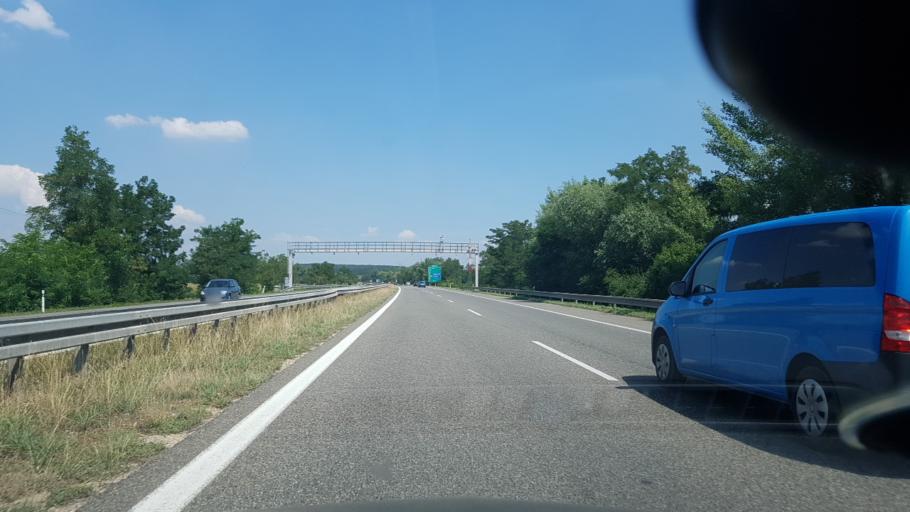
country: CZ
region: South Moravian
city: Pohorelice
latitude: 48.9850
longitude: 16.5433
